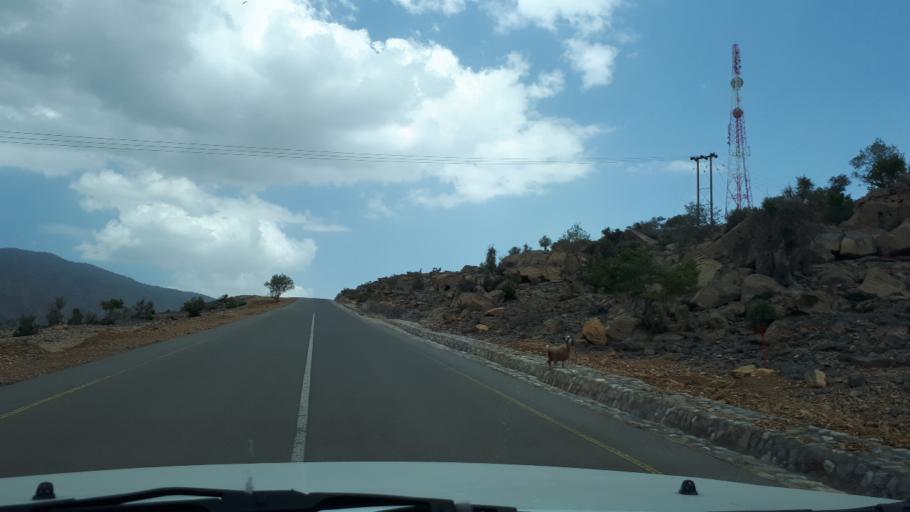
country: OM
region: Muhafazat ad Dakhiliyah
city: Bahla'
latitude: 23.2141
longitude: 57.2015
